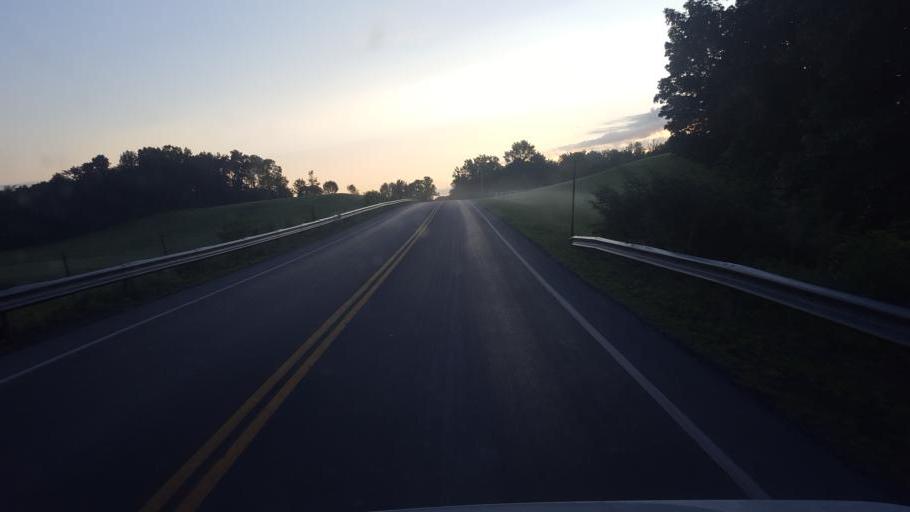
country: US
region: New York
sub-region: Wayne County
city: Clyde
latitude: 43.0566
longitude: -76.8979
